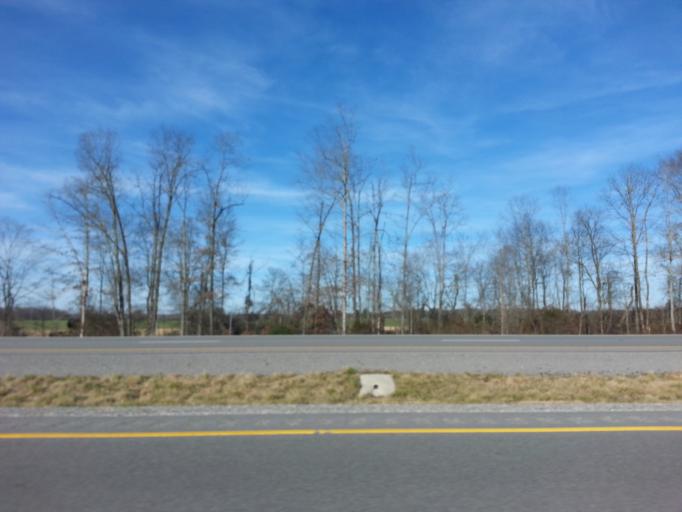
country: US
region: Tennessee
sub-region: Cannon County
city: Woodbury
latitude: 35.7512
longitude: -85.9550
